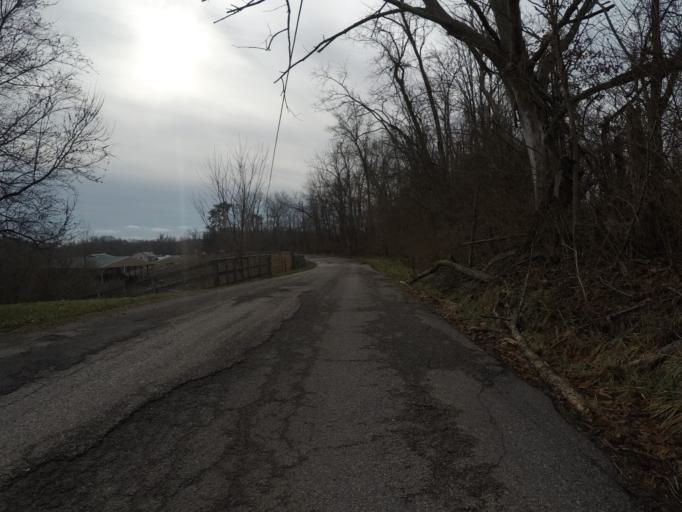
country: US
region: West Virginia
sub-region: Wayne County
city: Lavalette
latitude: 38.3630
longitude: -82.4126
